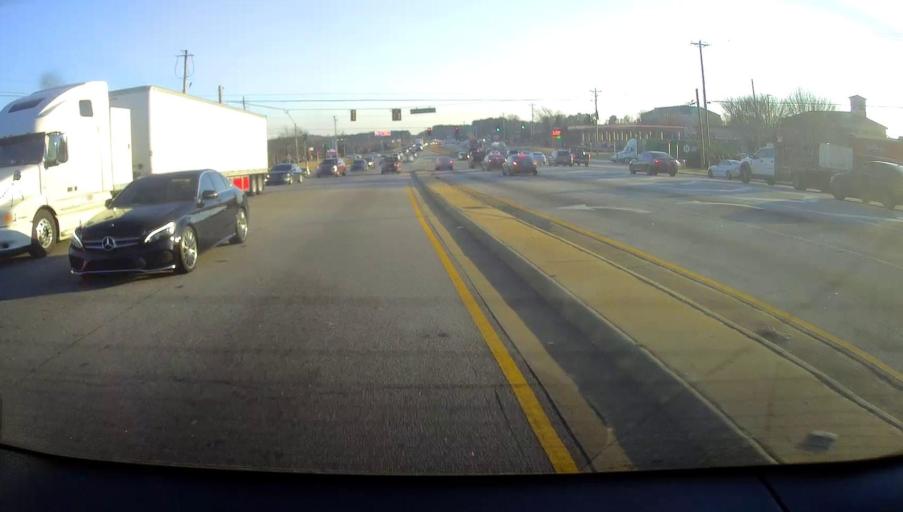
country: US
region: Georgia
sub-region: Fulton County
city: Fairburn
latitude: 33.5433
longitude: -84.5769
